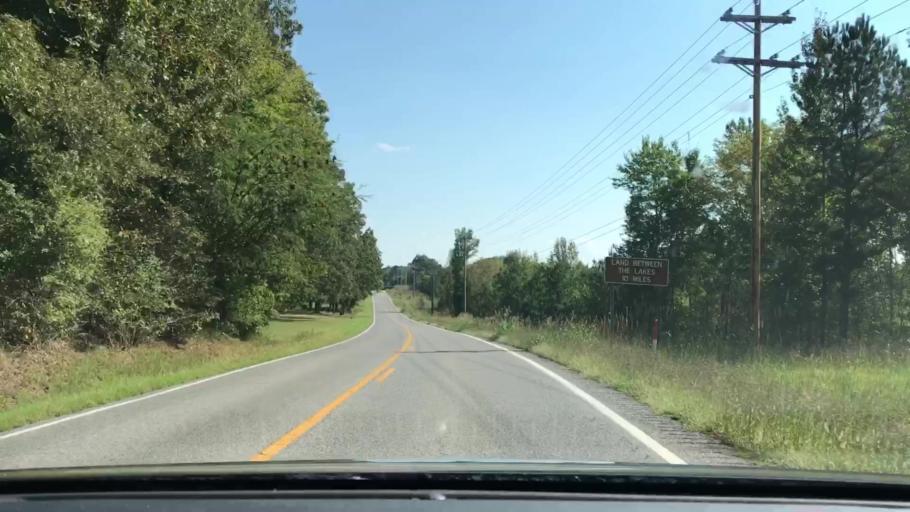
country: US
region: Kentucky
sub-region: Marshall County
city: Benton
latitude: 36.7642
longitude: -88.2594
